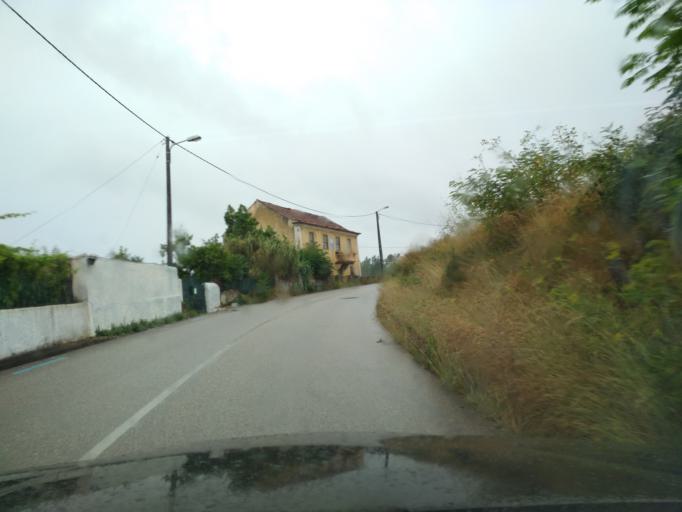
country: PT
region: Coimbra
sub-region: Coimbra
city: Coimbra
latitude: 40.1854
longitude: -8.4361
